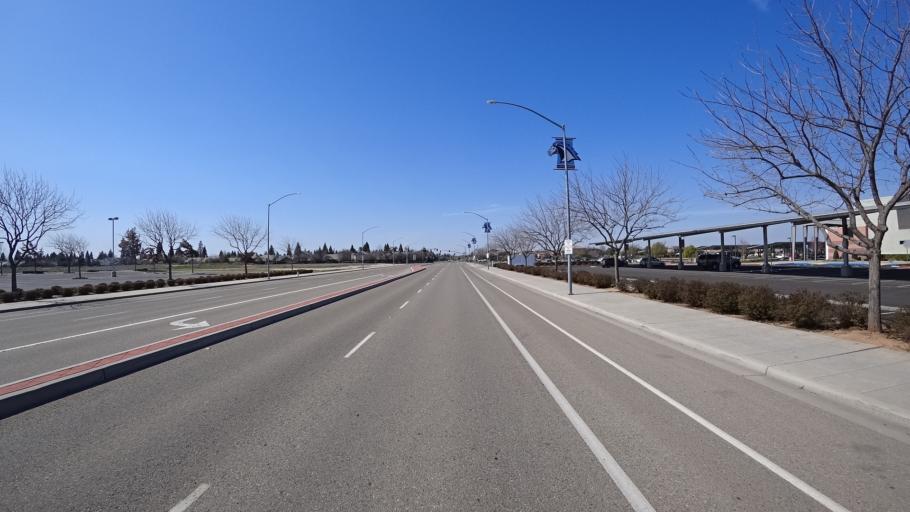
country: US
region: California
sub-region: Fresno County
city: Clovis
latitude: 36.8887
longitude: -119.7357
